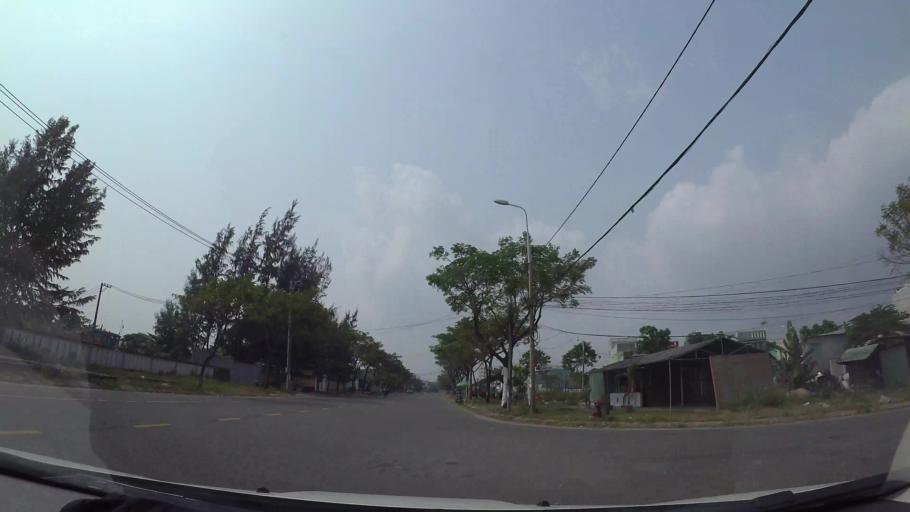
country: VN
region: Da Nang
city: Da Nang
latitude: 16.0987
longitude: 108.2344
